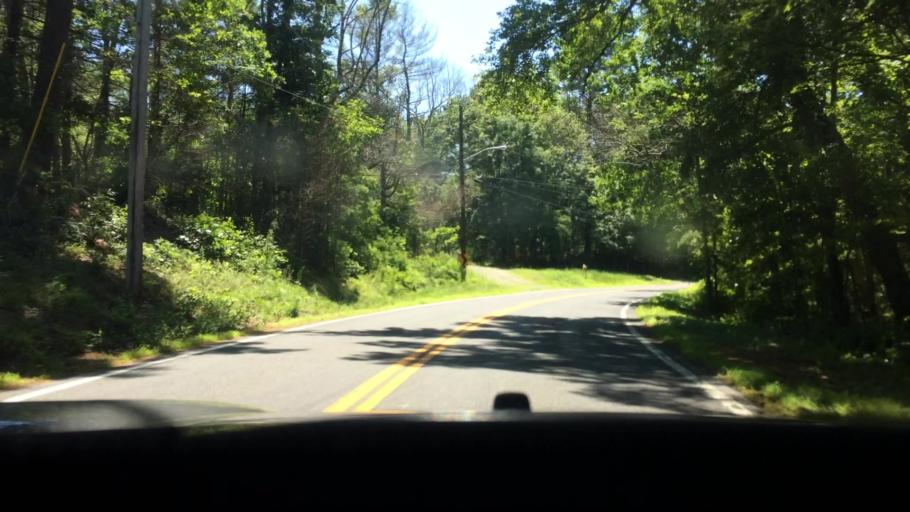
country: US
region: Rhode Island
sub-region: Providence County
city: Harrisville
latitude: 42.0082
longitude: -71.6767
